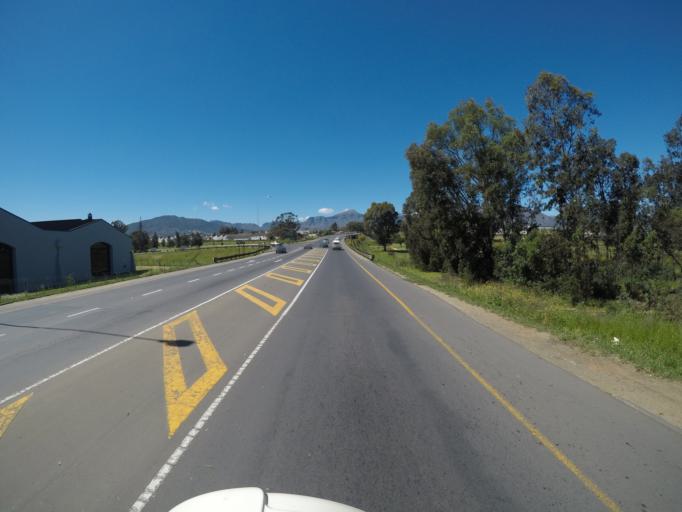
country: ZA
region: Western Cape
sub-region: Cape Winelands District Municipality
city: Noorder-Paarl
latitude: -33.6460
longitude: 18.9861
